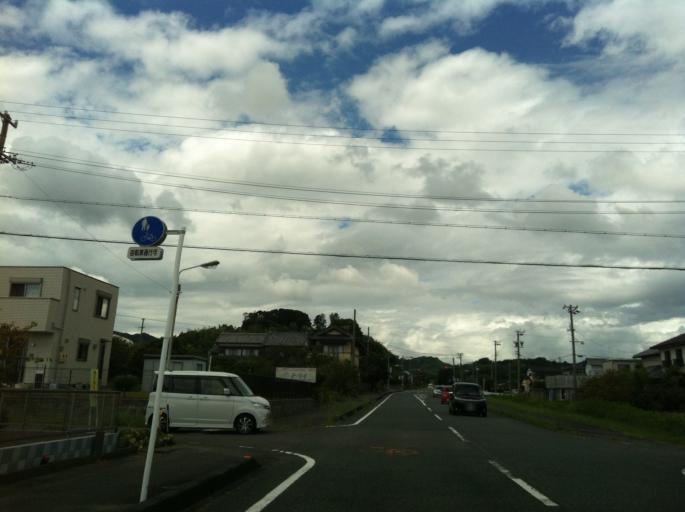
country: JP
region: Shizuoka
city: Kakegawa
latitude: 34.6806
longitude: 138.0441
